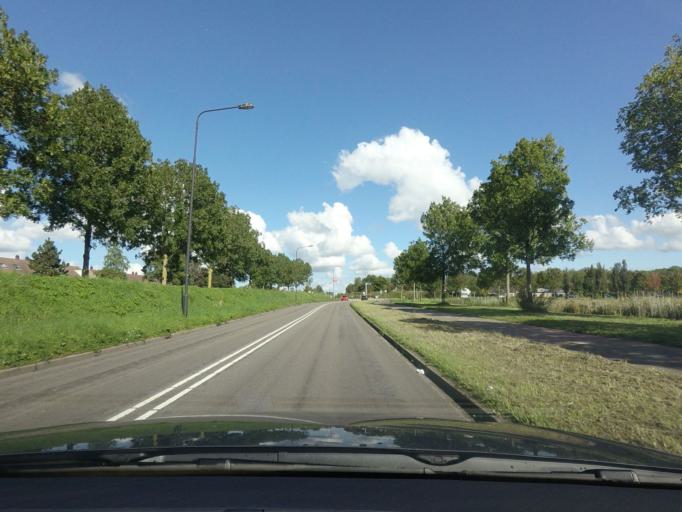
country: NL
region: North Holland
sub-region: Gemeente Heerhugowaard
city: Heerhugowaard
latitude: 52.6551
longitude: 4.8364
